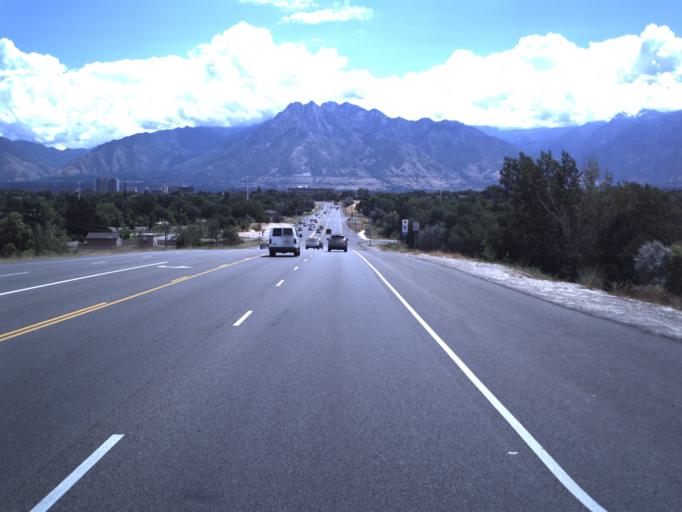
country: US
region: Utah
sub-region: Salt Lake County
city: Taylorsville
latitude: 40.6529
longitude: -111.9295
